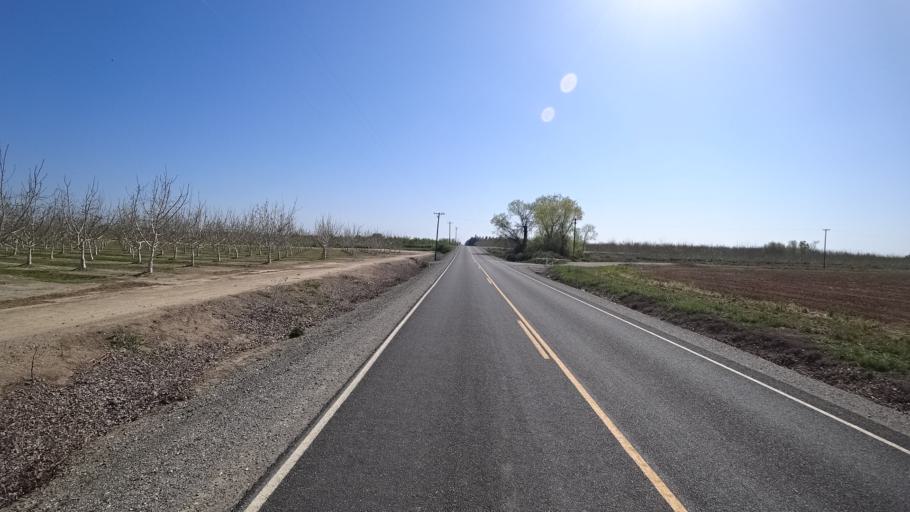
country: US
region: California
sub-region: Glenn County
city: Hamilton City
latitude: 39.6596
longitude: -122.0293
